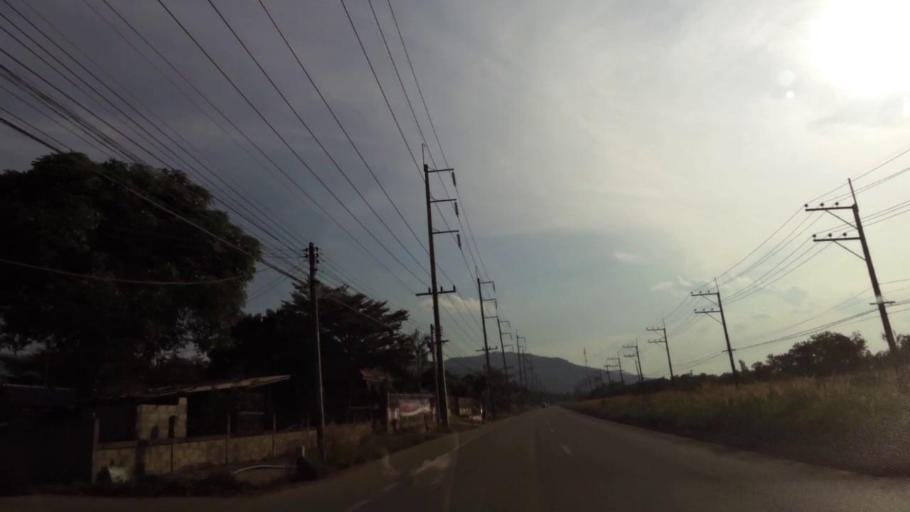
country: TH
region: Chiang Rai
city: Khun Tan
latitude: 19.8873
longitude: 100.2935
